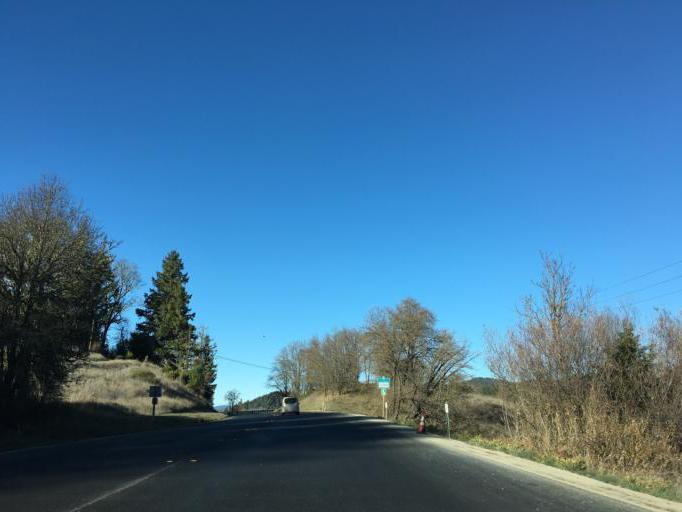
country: US
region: California
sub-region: Mendocino County
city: Laytonville
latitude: 39.6295
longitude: -123.4627
